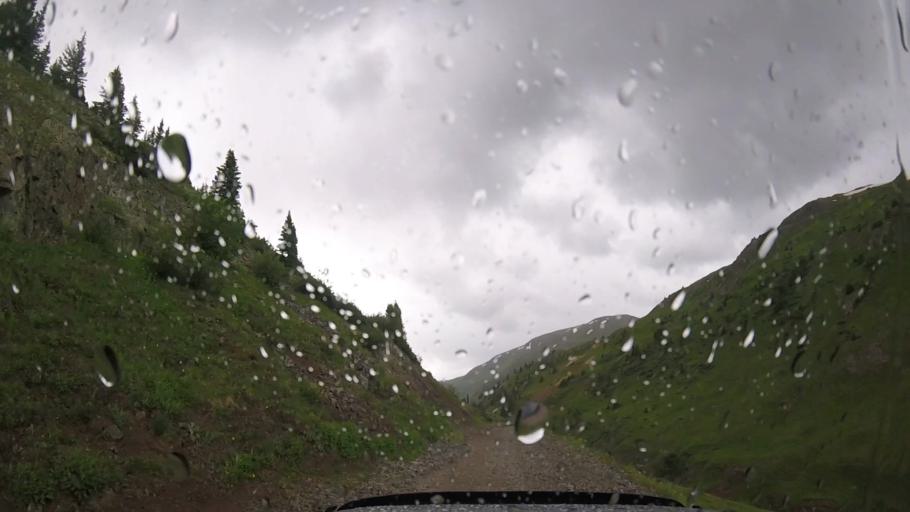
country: US
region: Colorado
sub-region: Ouray County
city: Ouray
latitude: 37.9426
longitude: -107.5736
